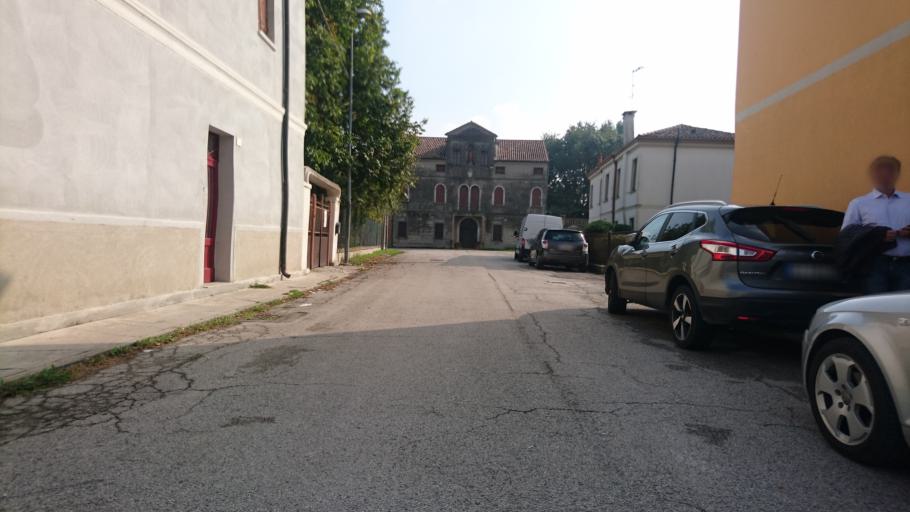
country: IT
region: Veneto
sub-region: Provincia di Rovigo
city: Grignano Polesine
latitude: 45.0414
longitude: 11.7512
